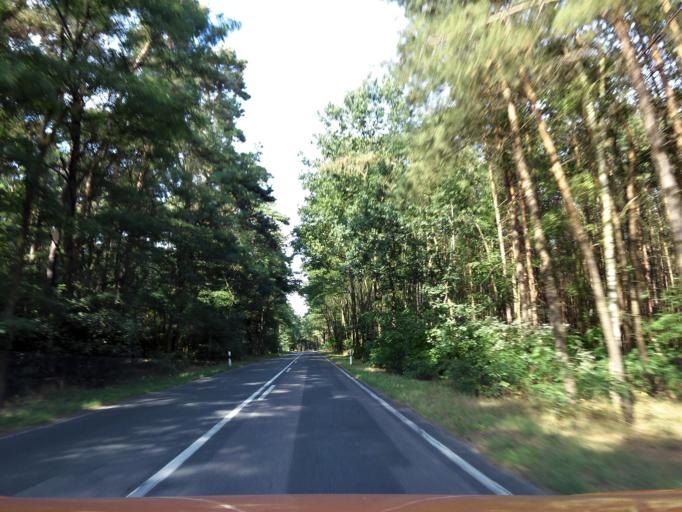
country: DE
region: Brandenburg
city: Michendorf
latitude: 52.2914
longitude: 13.1130
